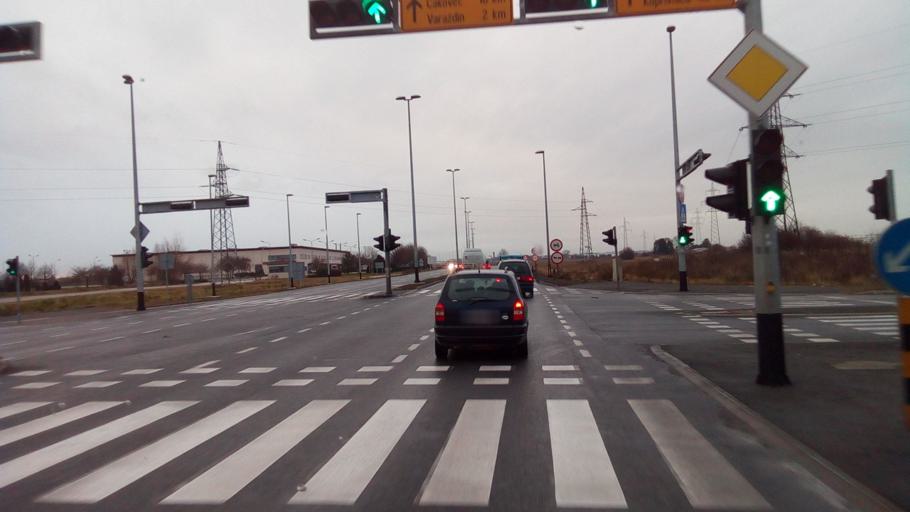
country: HR
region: Varazdinska
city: Varazdin
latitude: 46.2732
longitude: 16.3619
